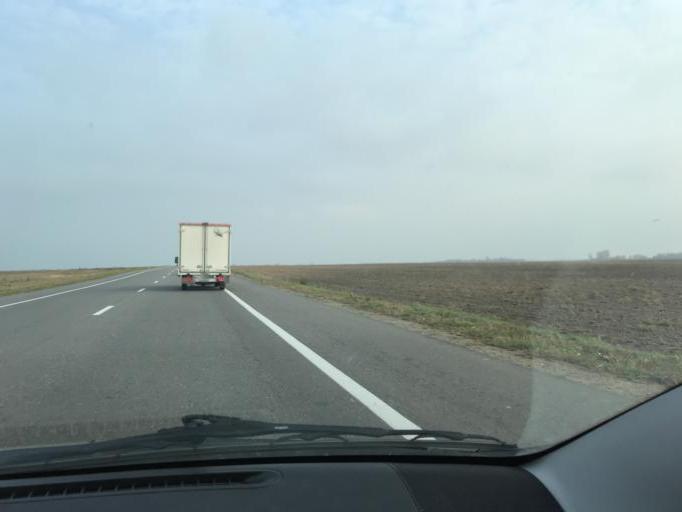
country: BY
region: Vitebsk
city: Syanno
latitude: 55.0967
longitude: 29.6584
